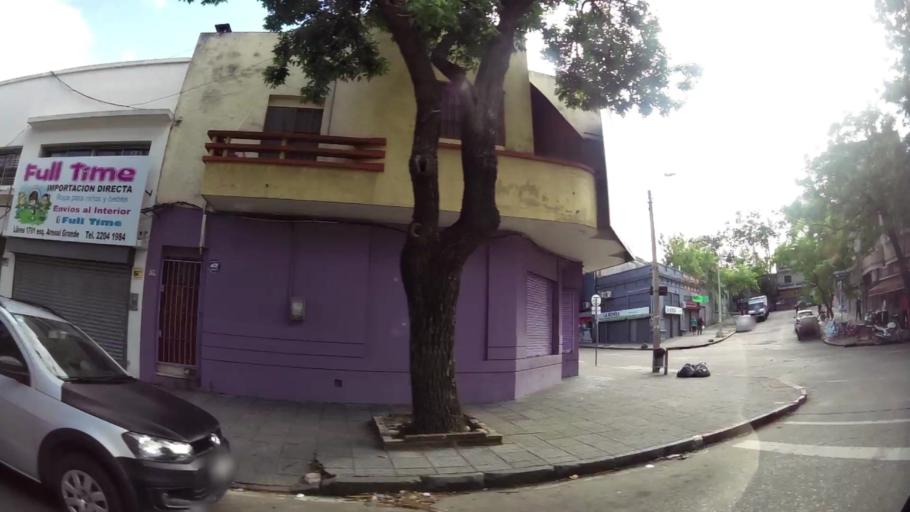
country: UY
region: Montevideo
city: Montevideo
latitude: -34.8864
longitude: -56.1804
